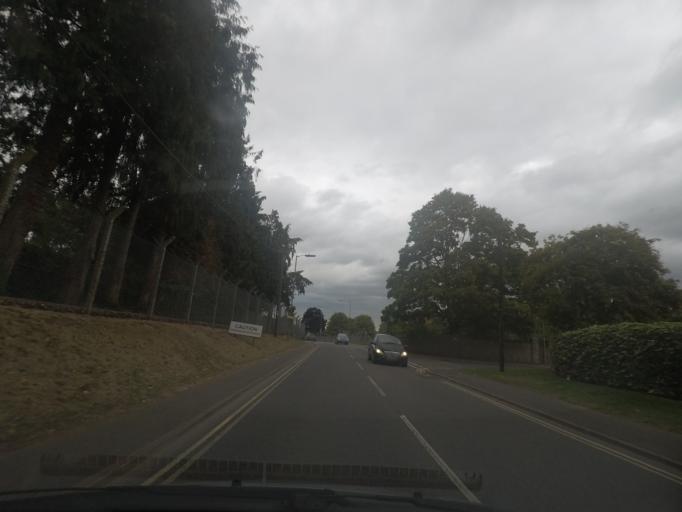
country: GB
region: England
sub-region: Oxfordshire
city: Didcot
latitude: 51.6112
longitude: -1.2522
